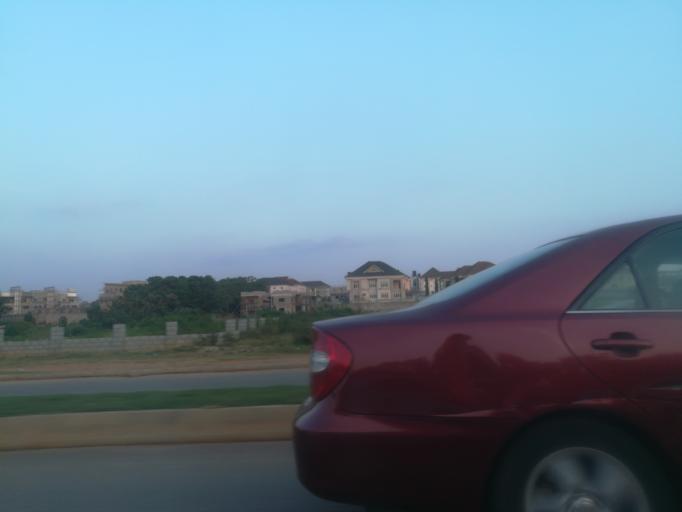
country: NG
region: Abuja Federal Capital Territory
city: Abuja
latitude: 9.0574
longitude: 7.4345
